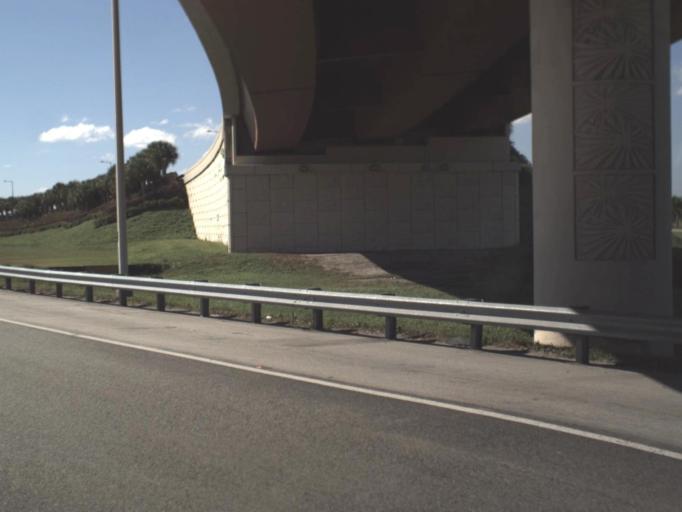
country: US
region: Florida
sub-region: Miami-Dade County
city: Sweetwater
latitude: 25.7761
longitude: -80.3861
